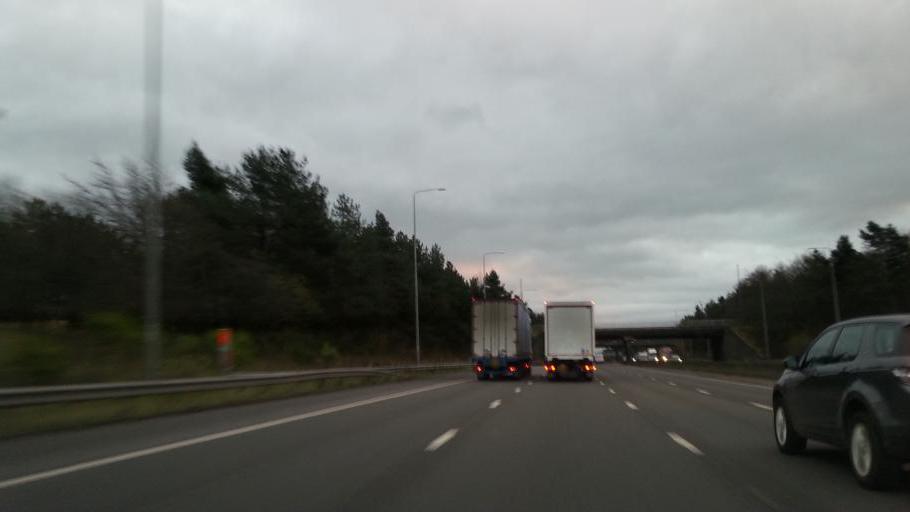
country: GB
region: England
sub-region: Nottinghamshire
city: Kirkby in Ashfield
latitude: 53.0652
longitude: -1.2710
